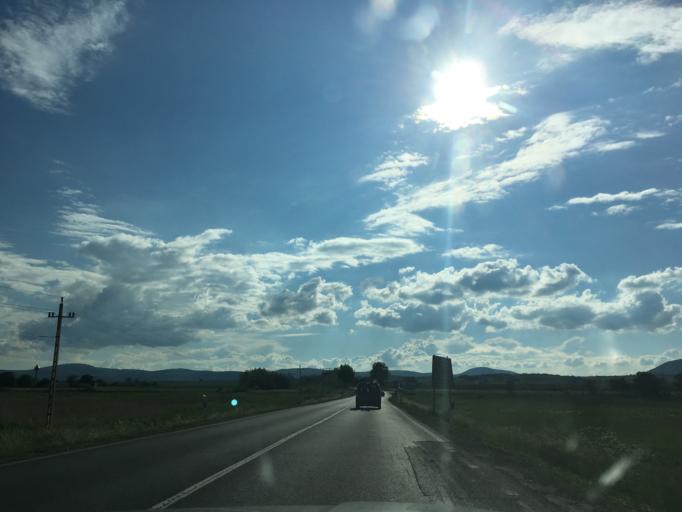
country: HU
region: Borsod-Abauj-Zemplen
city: Tolcsva
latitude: 48.2634
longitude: 21.4539
